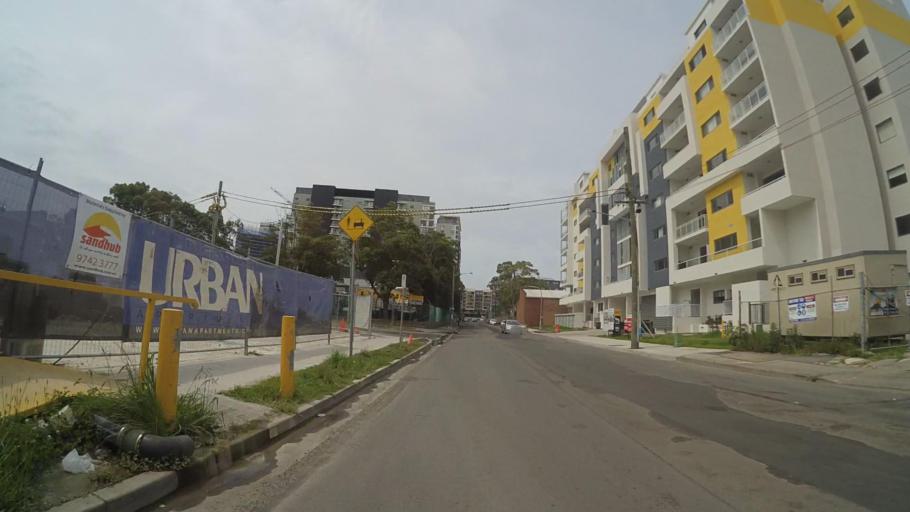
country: AU
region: New South Wales
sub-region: Rockdale
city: Arncliffe
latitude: -33.9318
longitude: 151.1515
